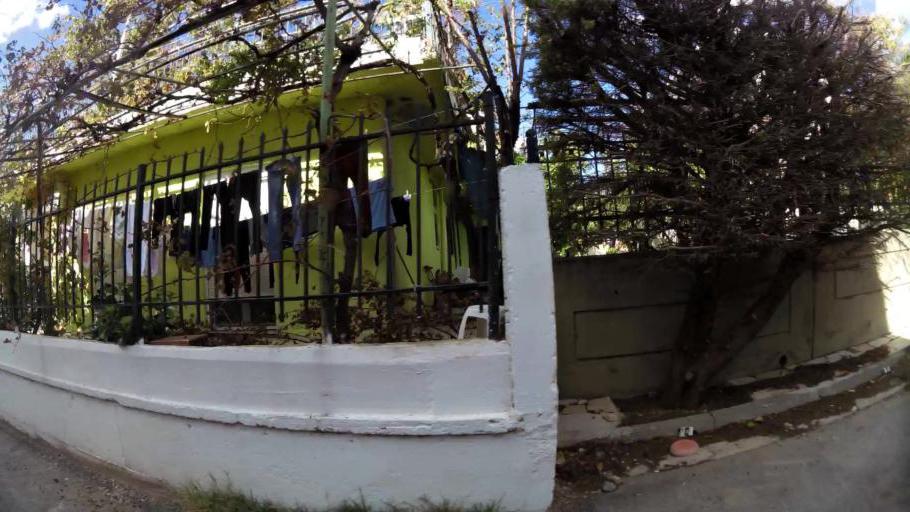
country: GR
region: Attica
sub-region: Nomarchia Anatolikis Attikis
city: Acharnes
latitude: 38.1006
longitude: 23.7318
